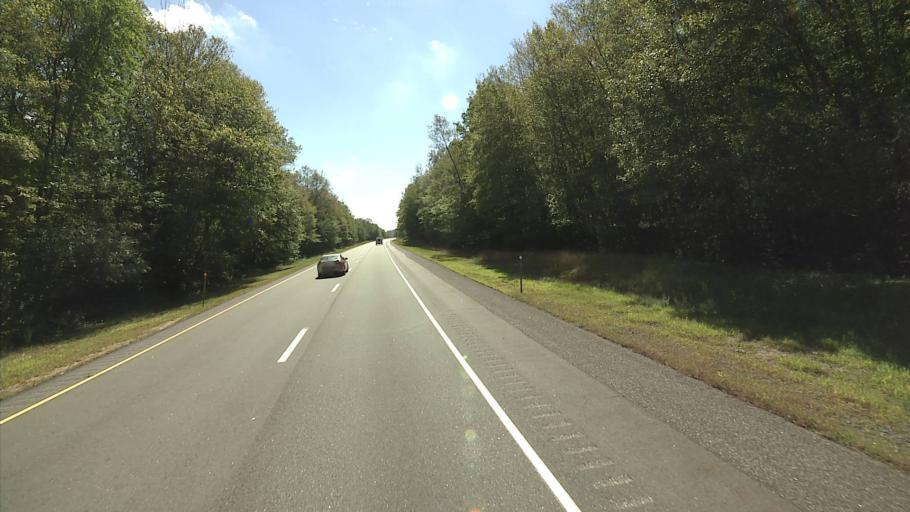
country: US
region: Connecticut
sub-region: New London County
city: Colchester
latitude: 41.5113
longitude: -72.3028
